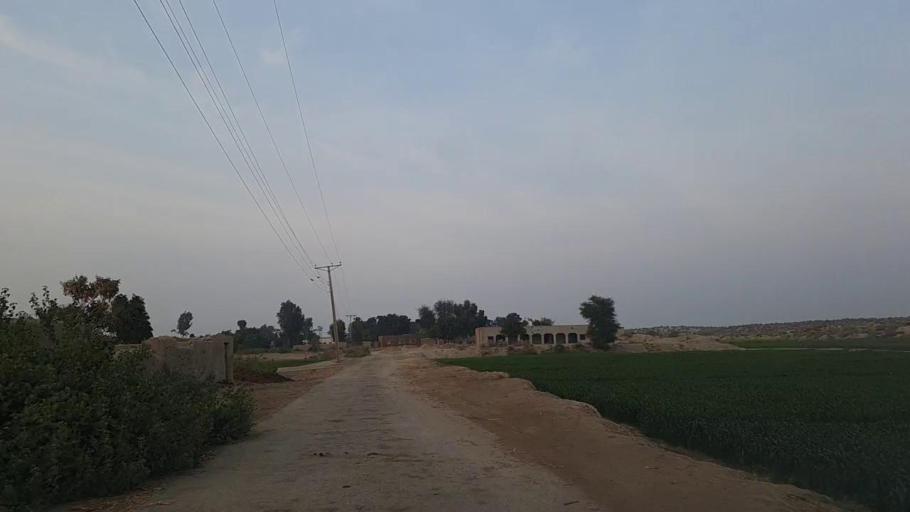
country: PK
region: Sindh
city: Jam Sahib
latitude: 26.4744
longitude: 68.5482
